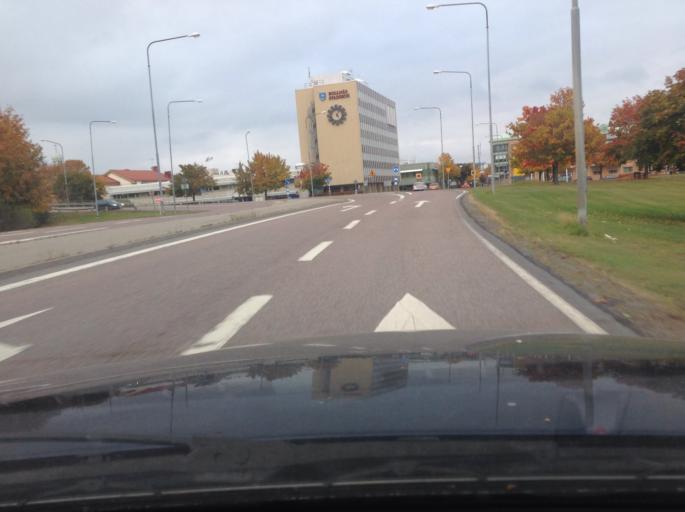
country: SE
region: Gaevleborg
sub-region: Bollnas Kommun
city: Bollnas
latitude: 61.3454
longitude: 16.3921
